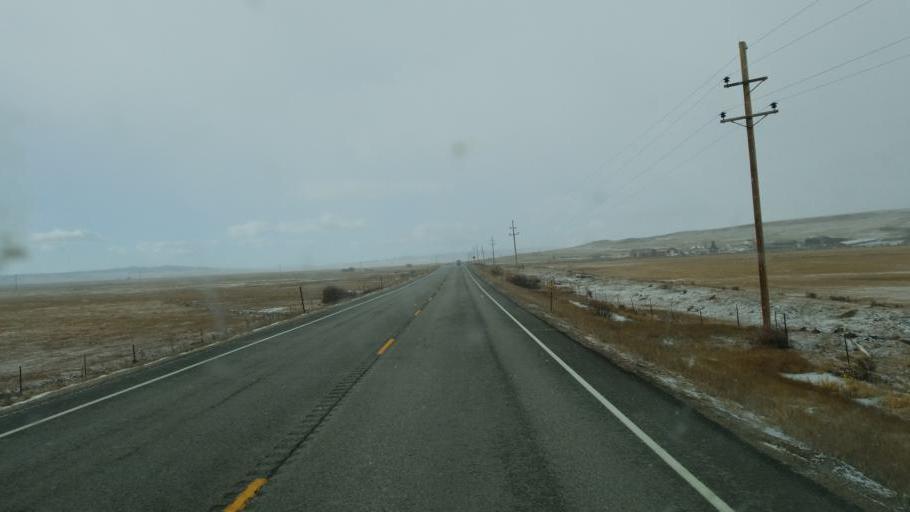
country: US
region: Colorado
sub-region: Summit County
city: Breckenridge
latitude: 39.3964
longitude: -105.7841
